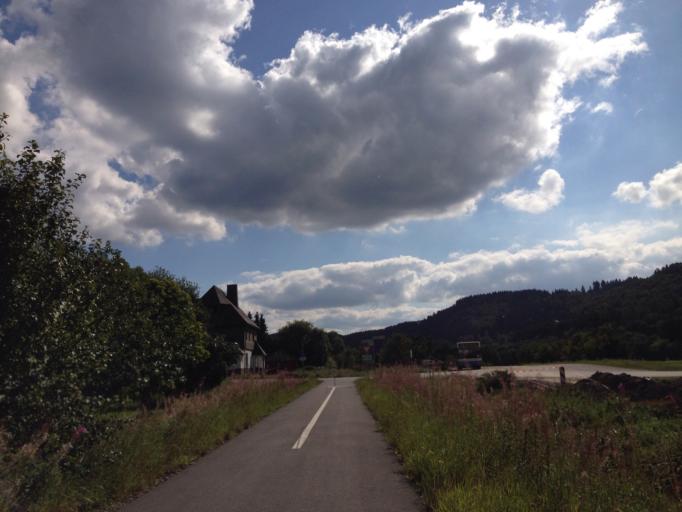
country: DE
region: Hesse
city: Hatzfeld
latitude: 51.0117
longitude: 8.5850
